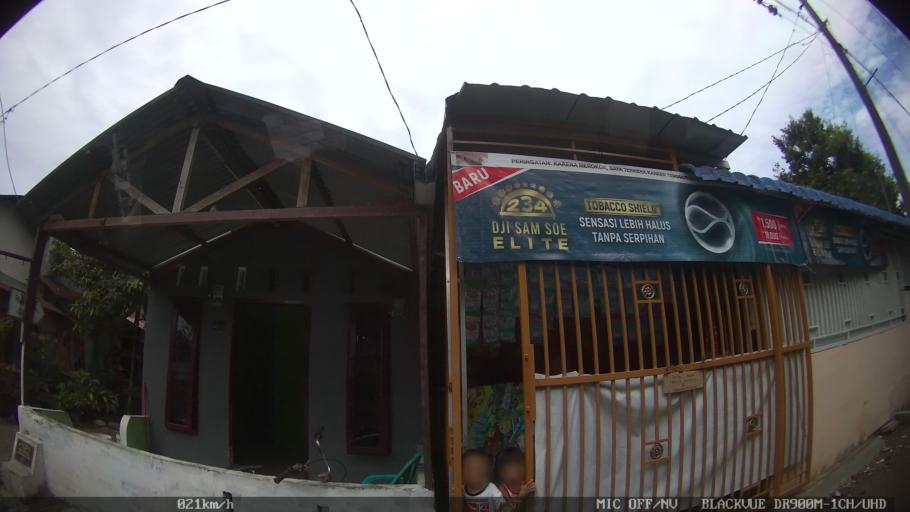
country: ID
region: North Sumatra
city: Sunggal
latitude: 3.6490
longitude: 98.5922
